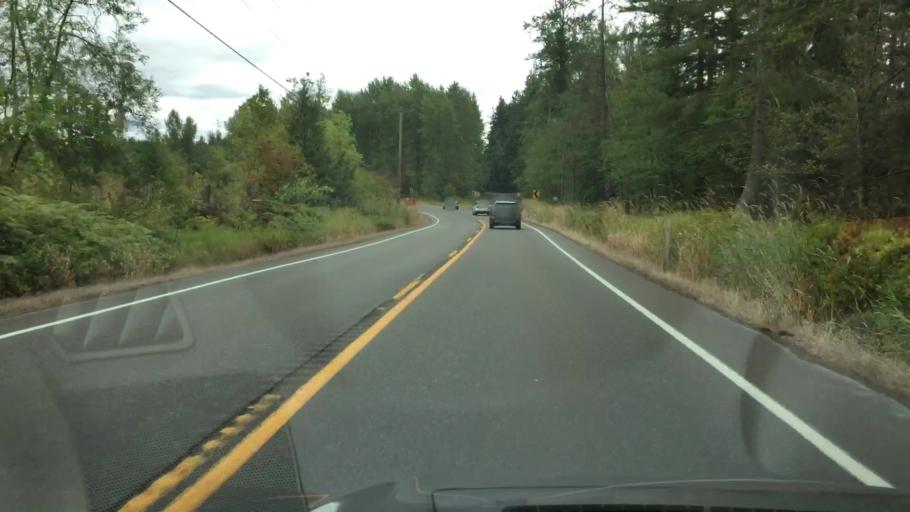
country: US
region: Washington
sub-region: Pierce County
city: Eatonville
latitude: 46.9544
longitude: -122.2972
